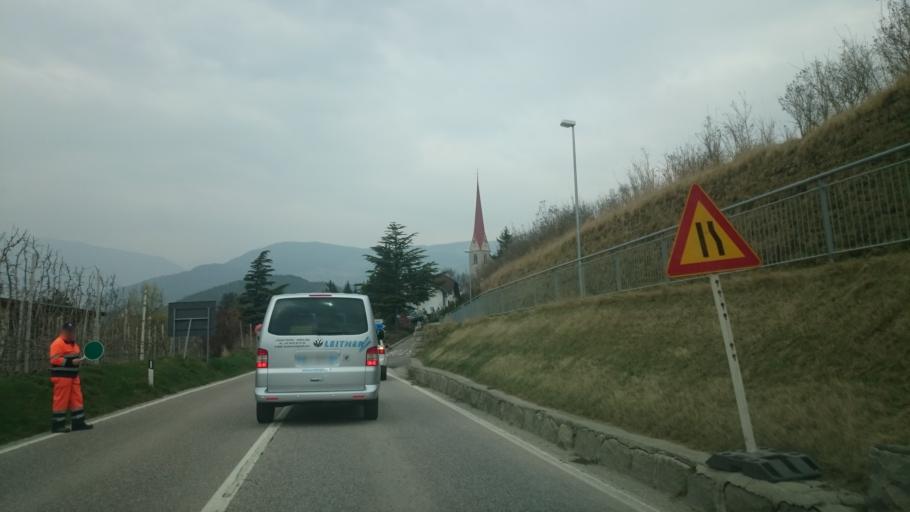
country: IT
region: Trentino-Alto Adige
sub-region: Bolzano
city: Naz-Sciaves - Natz-Schabs
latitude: 46.7679
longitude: 11.6630
